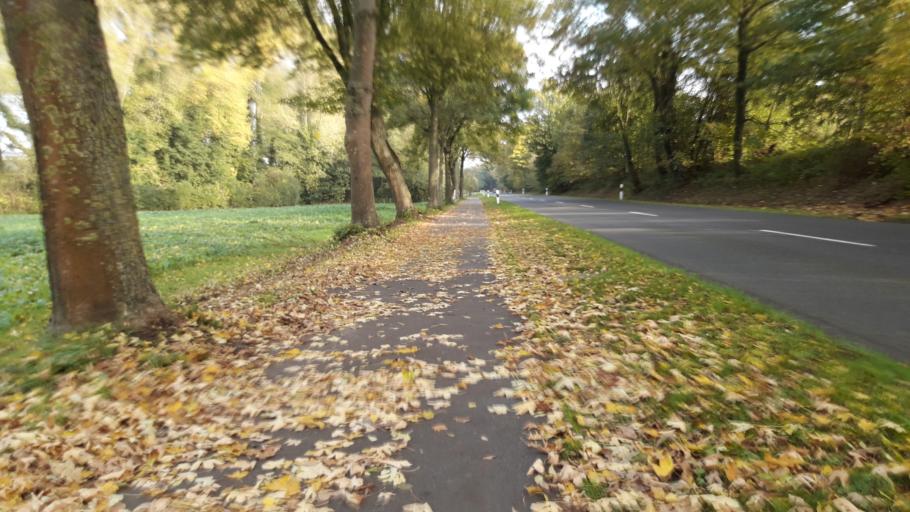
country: DE
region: North Rhine-Westphalia
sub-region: Regierungsbezirk Detmold
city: Paderborn
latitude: 51.6757
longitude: 8.7031
